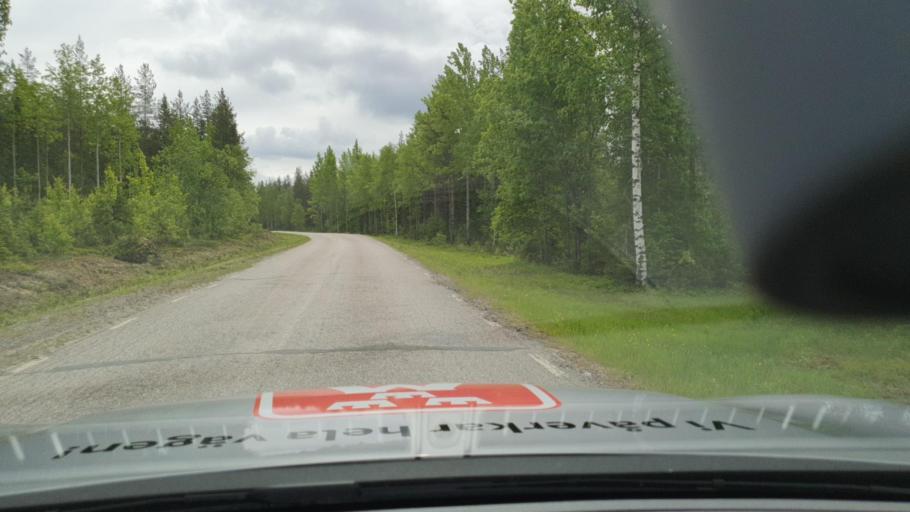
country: SE
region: Norrbotten
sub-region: Kalix Kommun
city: Kalix
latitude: 66.0542
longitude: 23.2181
